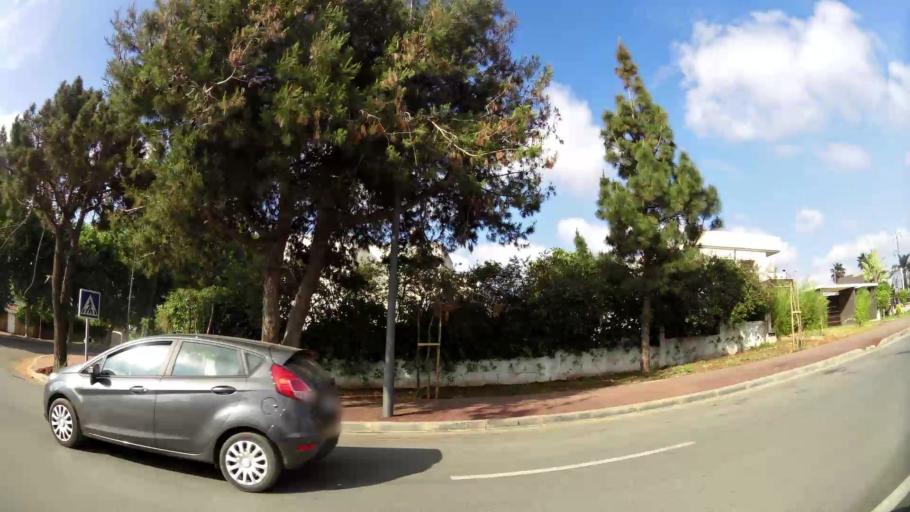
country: MA
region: Rabat-Sale-Zemmour-Zaer
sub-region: Skhirate-Temara
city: Temara
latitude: 33.9577
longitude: -6.8603
